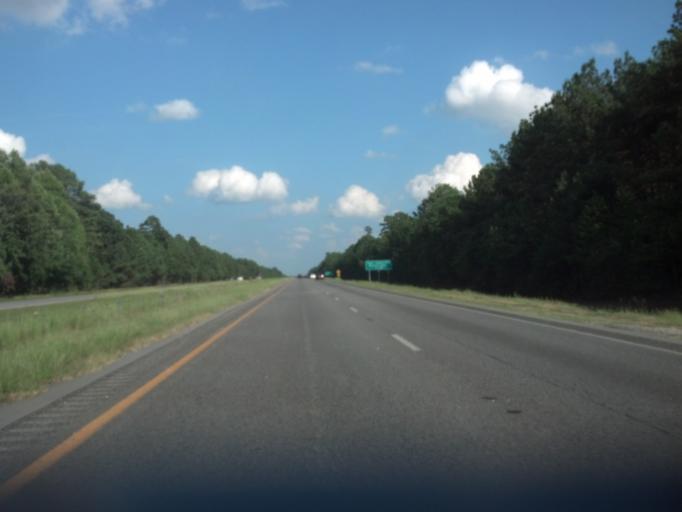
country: US
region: North Carolina
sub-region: Nash County
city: Rocky Mount
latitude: 35.9325
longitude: -77.7093
